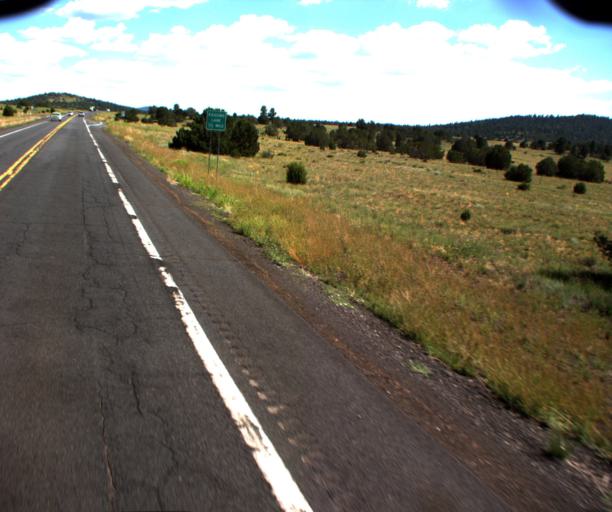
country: US
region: Arizona
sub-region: Coconino County
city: Williams
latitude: 35.3194
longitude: -112.1512
